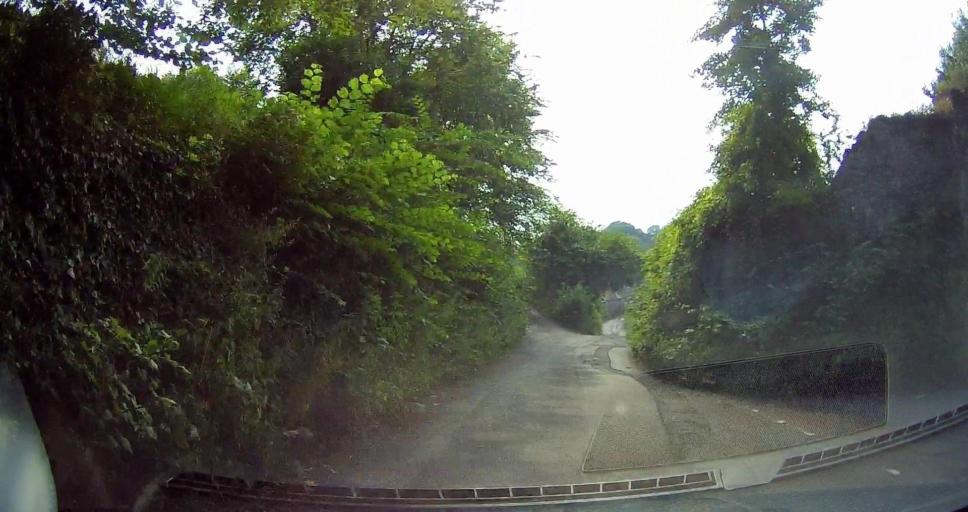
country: GB
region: England
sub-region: Borough of Torbay
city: Paignton
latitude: 50.4201
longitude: -3.5963
